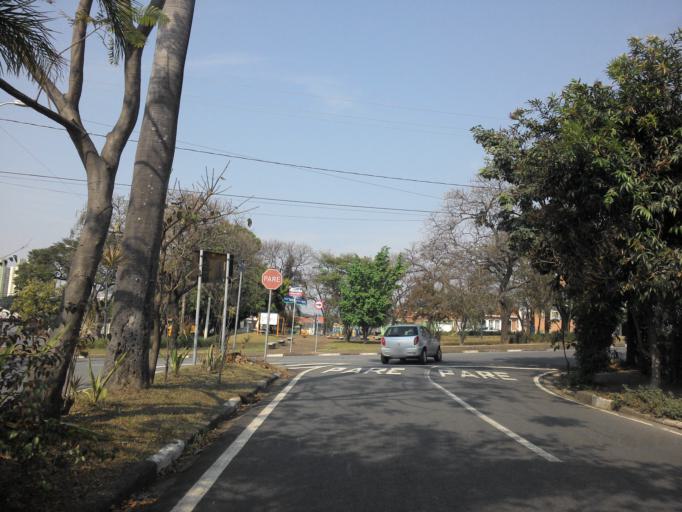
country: BR
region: Sao Paulo
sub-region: Campinas
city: Campinas
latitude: -22.9102
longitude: -47.0860
